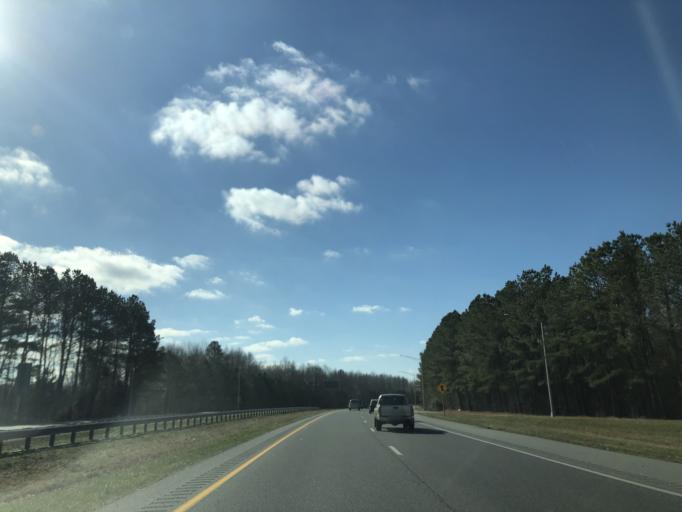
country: US
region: Maryland
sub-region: Worcester County
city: Berlin
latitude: 38.3750
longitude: -75.2065
